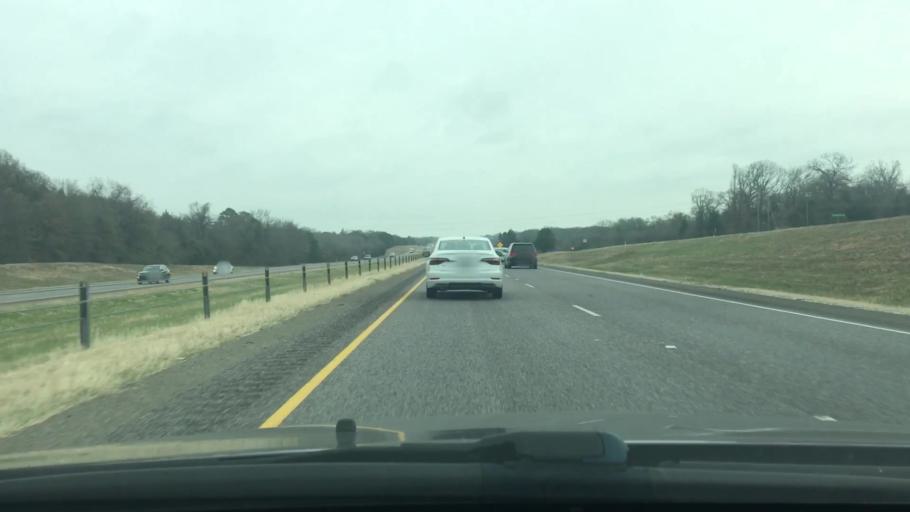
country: US
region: Texas
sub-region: Freestone County
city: Fairfield
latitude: 31.7541
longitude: -96.2035
